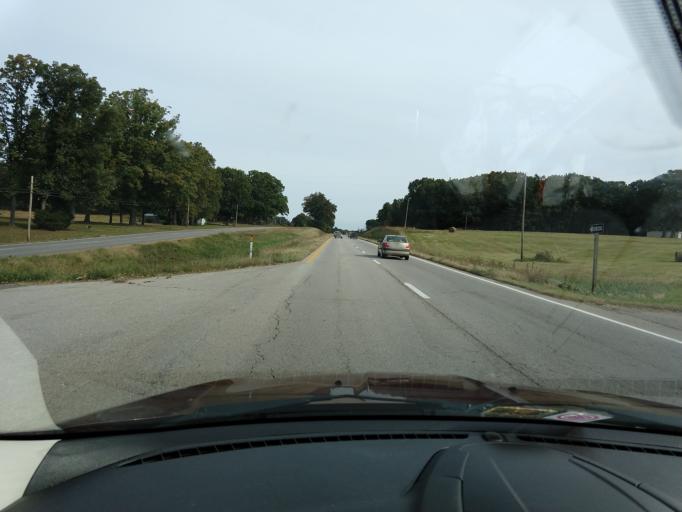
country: US
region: Virginia
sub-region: Pittsylvania County
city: Gretna
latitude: 36.9021
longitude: -79.3907
